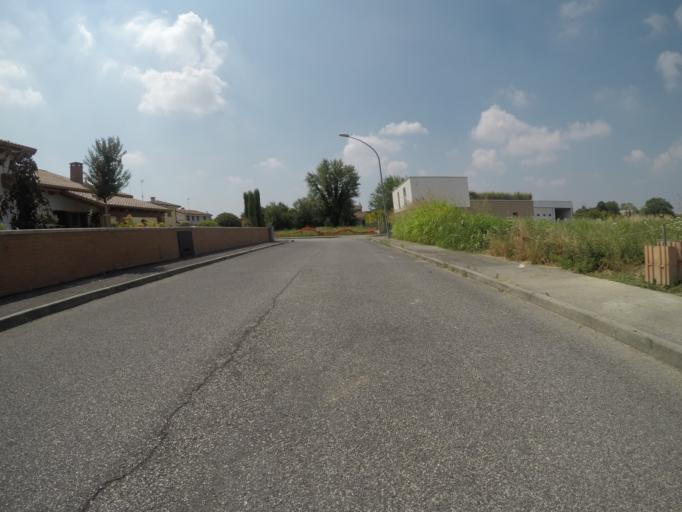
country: IT
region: Veneto
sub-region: Provincia di Rovigo
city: Fratta Polesine
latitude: 45.0323
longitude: 11.6481
